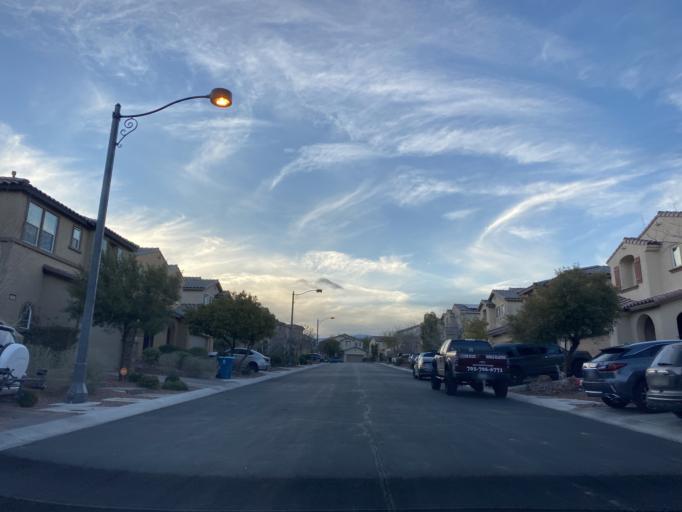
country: US
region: Nevada
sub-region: Clark County
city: Summerlin South
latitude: 36.3049
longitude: -115.3231
